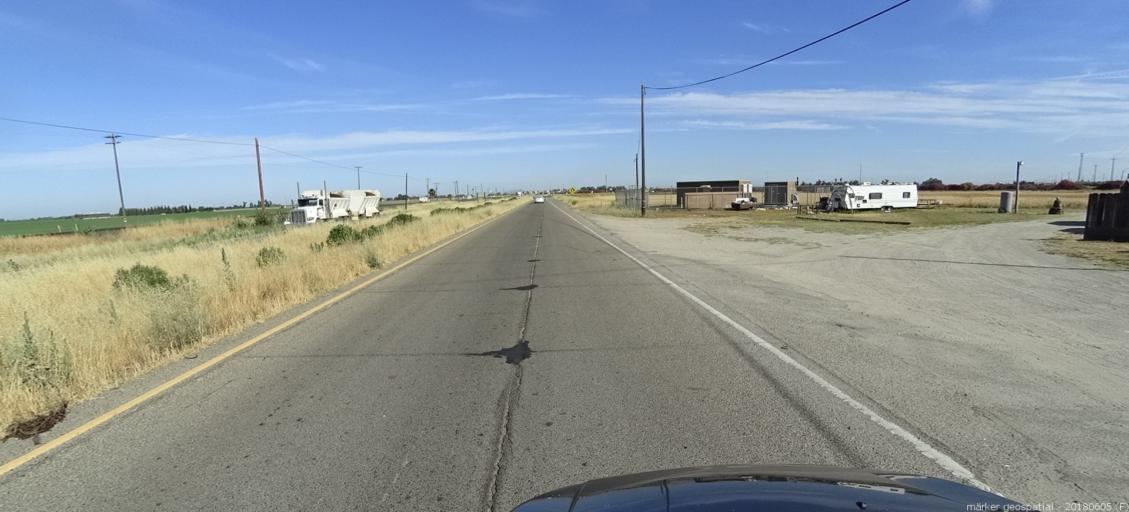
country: US
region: California
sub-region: Madera County
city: Chowchilla
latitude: 37.1398
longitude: -120.2750
